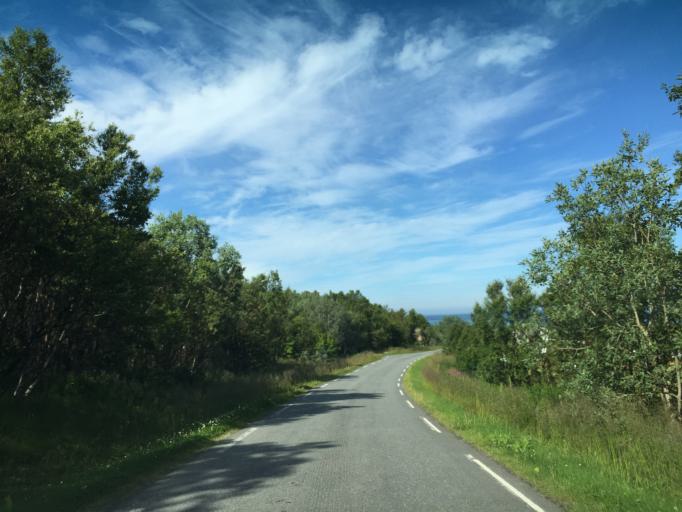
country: NO
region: Nordland
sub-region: Vagan
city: Svolvaer
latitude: 68.4015
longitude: 14.5223
